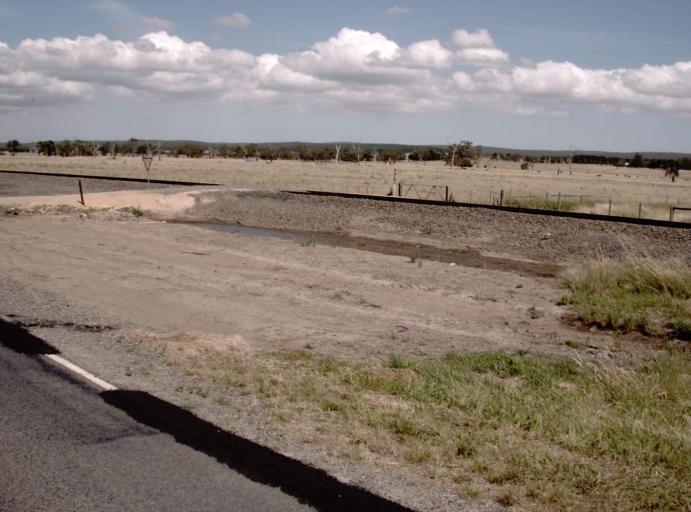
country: AU
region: Victoria
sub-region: Wellington
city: Heyfield
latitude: -38.1547
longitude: 146.8169
